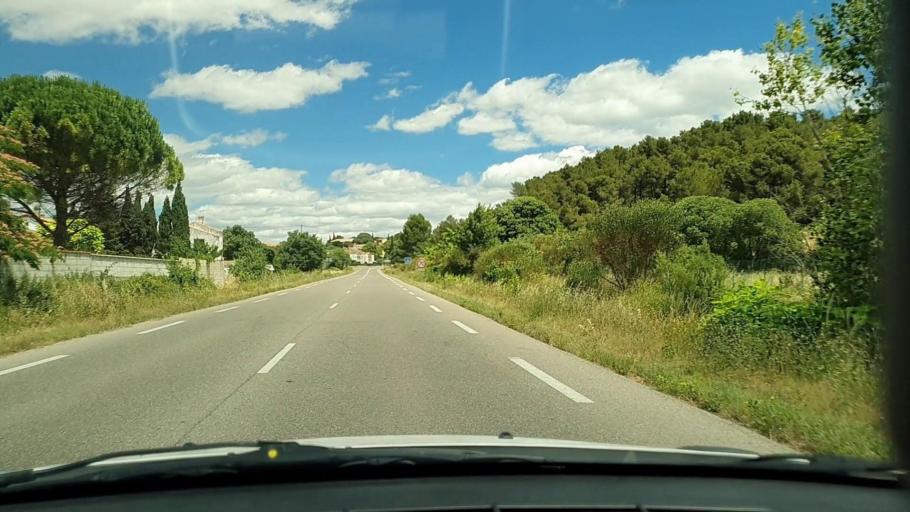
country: FR
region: Languedoc-Roussillon
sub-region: Departement du Gard
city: Marguerittes
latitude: 43.8649
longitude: 4.4040
